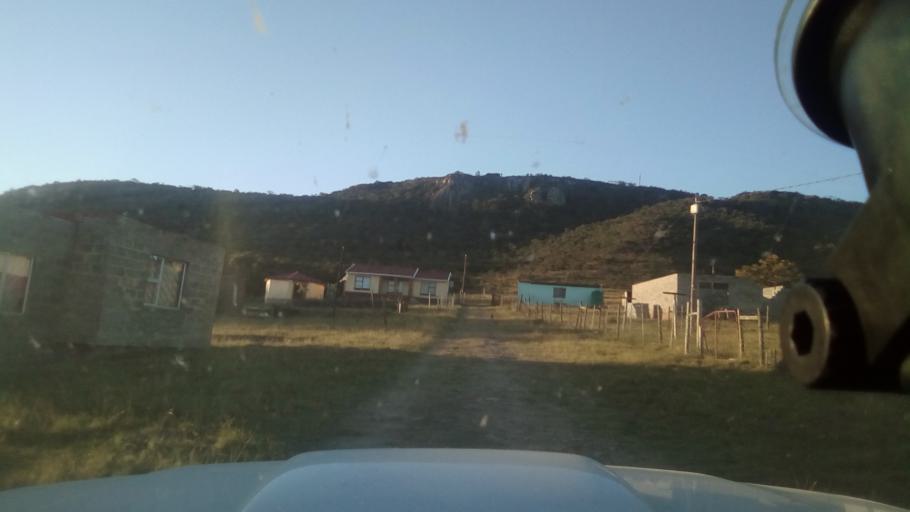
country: ZA
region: Eastern Cape
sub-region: Buffalo City Metropolitan Municipality
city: Bhisho
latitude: -32.7340
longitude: 27.3778
